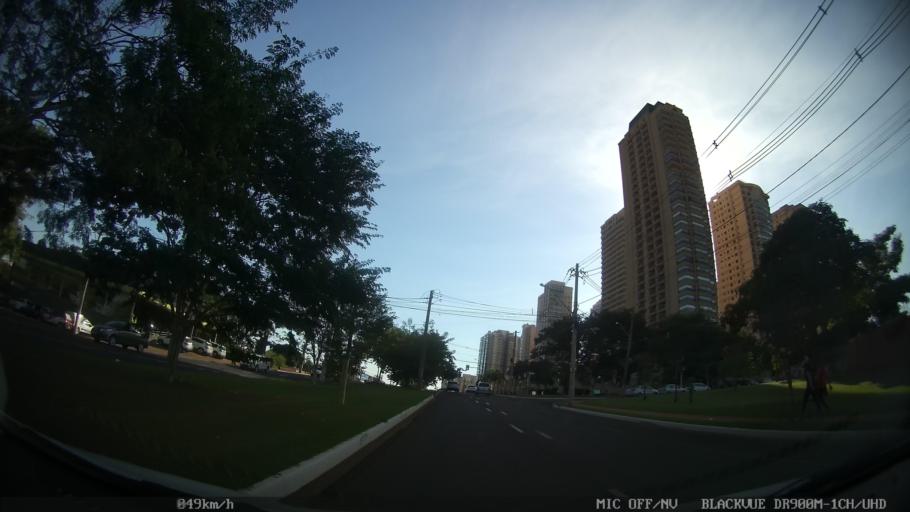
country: BR
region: Sao Paulo
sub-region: Ribeirao Preto
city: Ribeirao Preto
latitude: -21.2202
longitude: -47.8059
